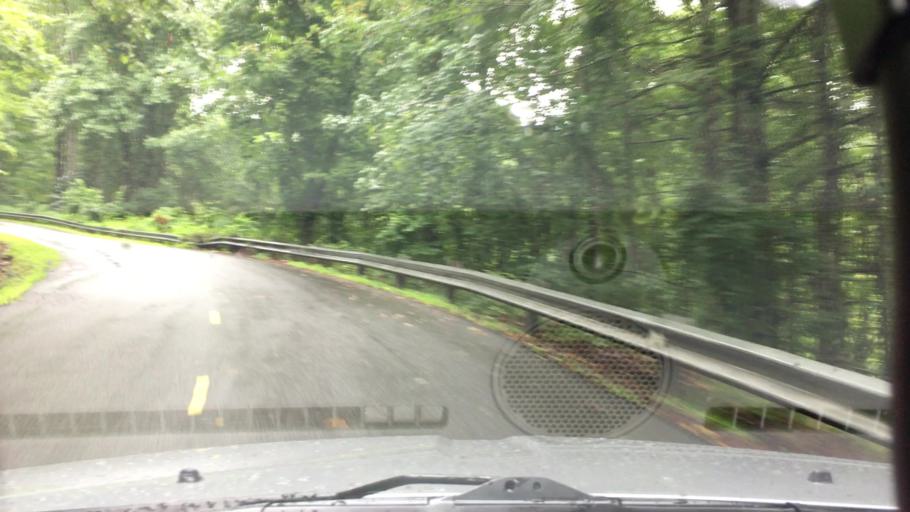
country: US
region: North Carolina
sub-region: Madison County
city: Mars Hill
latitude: 35.9446
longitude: -82.5240
